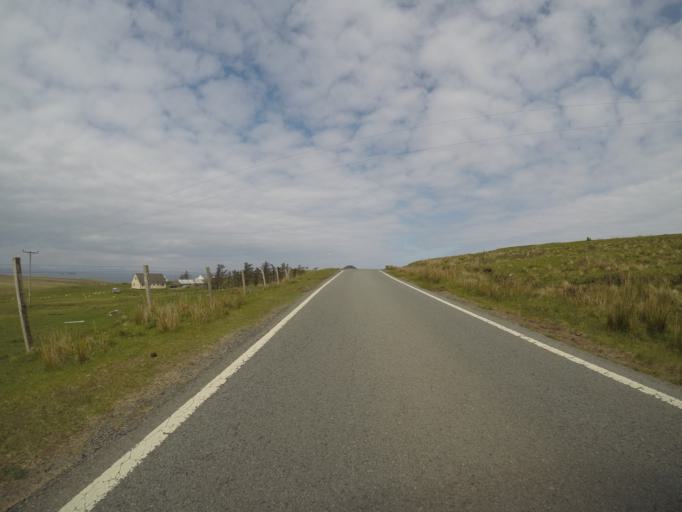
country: GB
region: Scotland
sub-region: Highland
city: Portree
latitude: 57.6528
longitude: -6.3800
